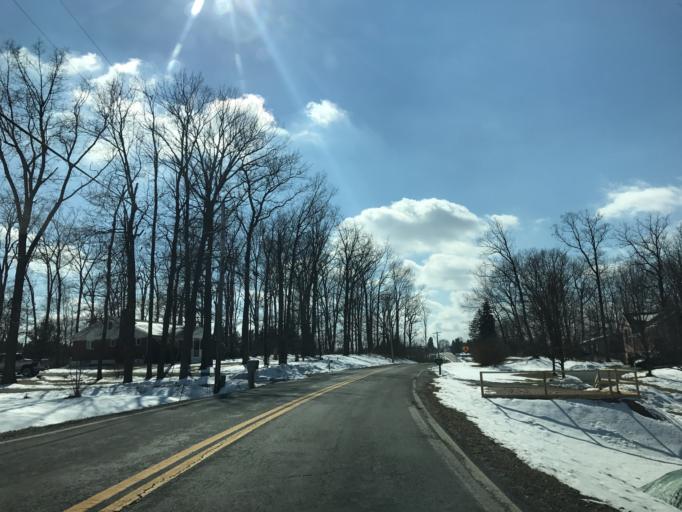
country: US
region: Maryland
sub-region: Carroll County
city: Manchester
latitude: 39.6779
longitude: -76.8653
